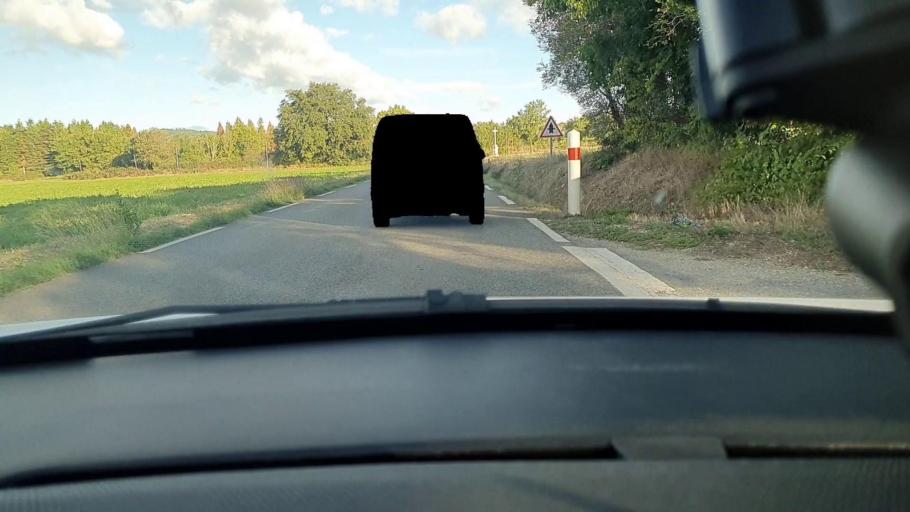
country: FR
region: Languedoc-Roussillon
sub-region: Departement du Gard
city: Saint-Ambroix
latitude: 44.2453
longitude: 4.2181
